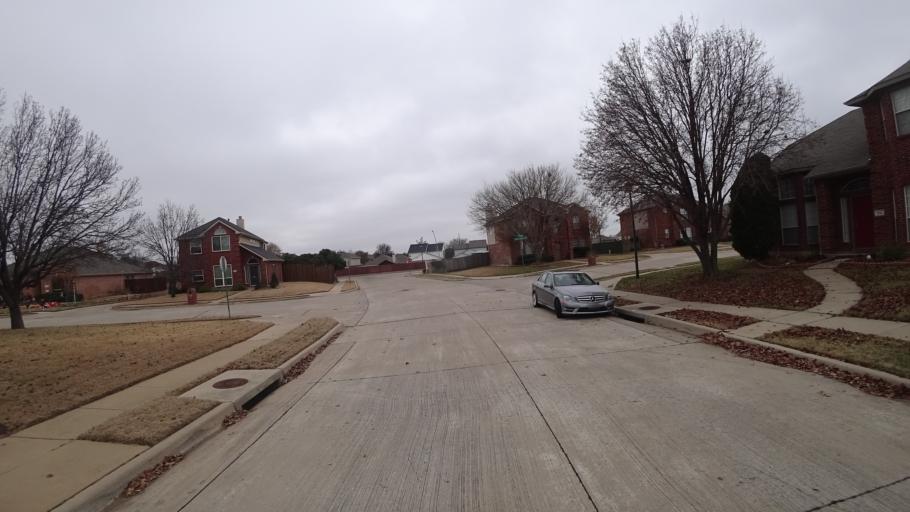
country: US
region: Texas
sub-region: Denton County
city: Lewisville
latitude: 33.0364
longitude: -97.0346
